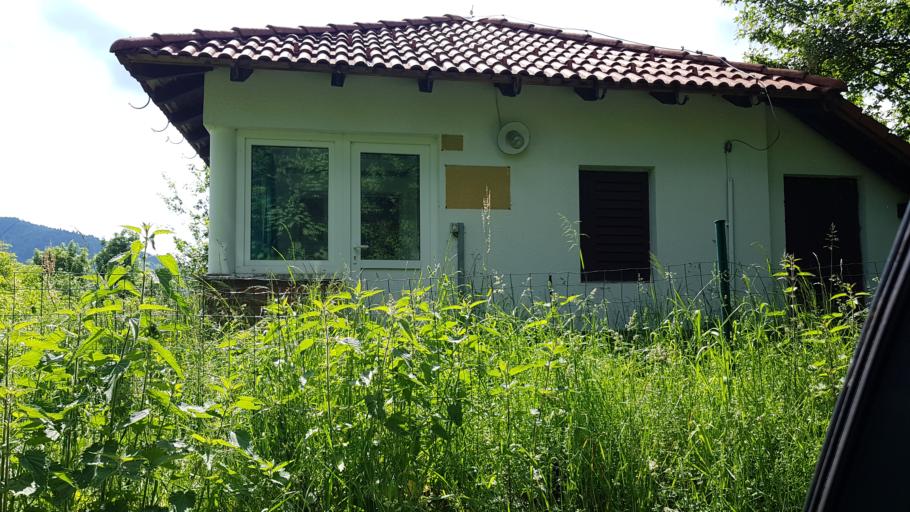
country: IT
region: Friuli Venezia Giulia
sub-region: Provincia di Udine
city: Pulfero
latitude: 46.2138
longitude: 13.4147
